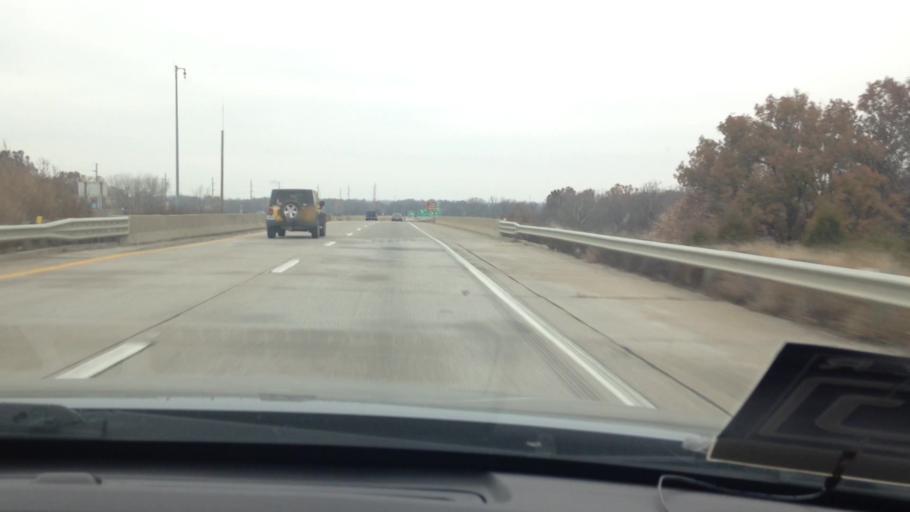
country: US
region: Missouri
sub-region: Cass County
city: Harrisonville
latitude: 38.6451
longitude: -94.3614
